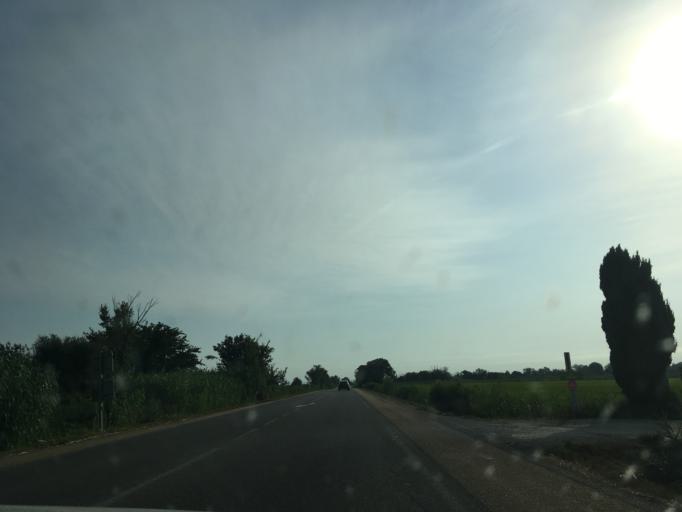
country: FR
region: Languedoc-Roussillon
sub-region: Departement du Gard
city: Saint-Gilles
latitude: 43.6158
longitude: 4.4837
